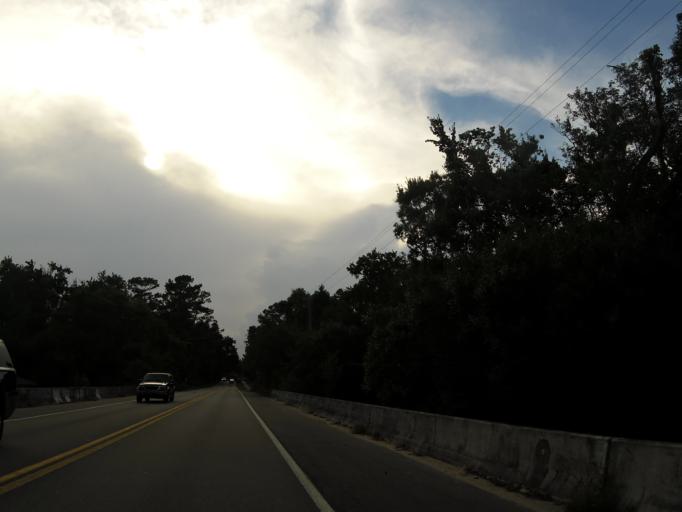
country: US
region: Florida
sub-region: Saint Johns County
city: Fruit Cove
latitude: 30.1403
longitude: -81.6211
